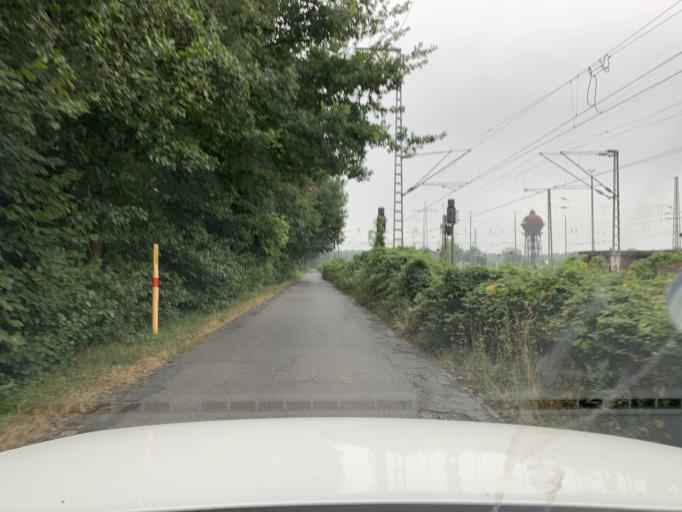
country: DE
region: North Rhine-Westphalia
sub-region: Regierungsbezirk Dusseldorf
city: Duisburg
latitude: 51.3853
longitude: 6.8116
